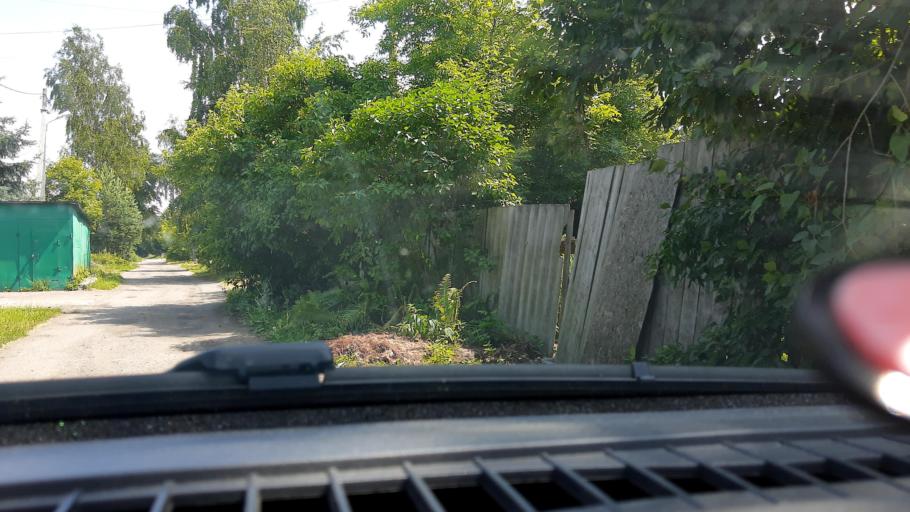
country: RU
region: Nizjnij Novgorod
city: Gorbatovka
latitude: 56.2717
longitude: 43.7518
